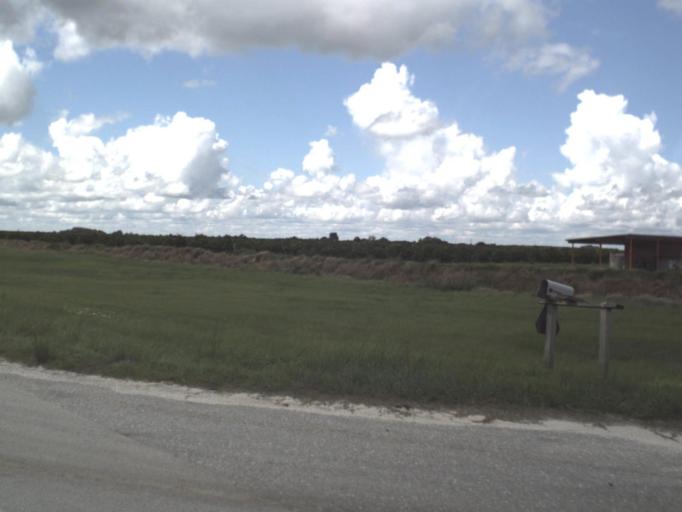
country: US
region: Florida
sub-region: Highlands County
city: Placid Lakes
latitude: 27.2097
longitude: -81.5795
